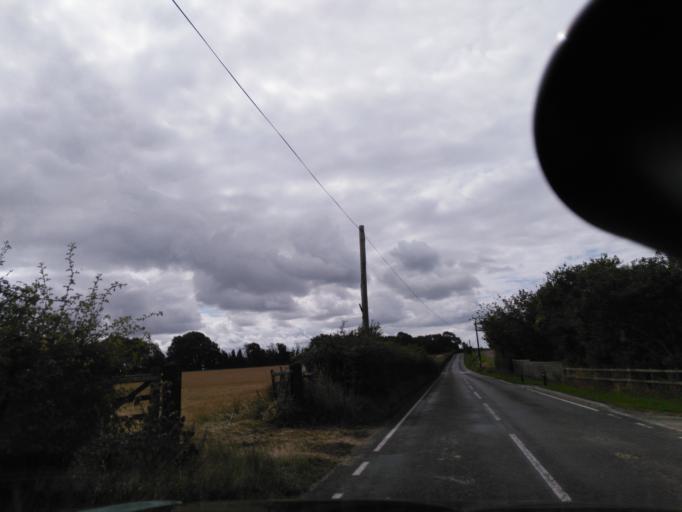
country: GB
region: England
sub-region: Dorset
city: Blandford Forum
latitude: 50.8994
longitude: -2.1553
